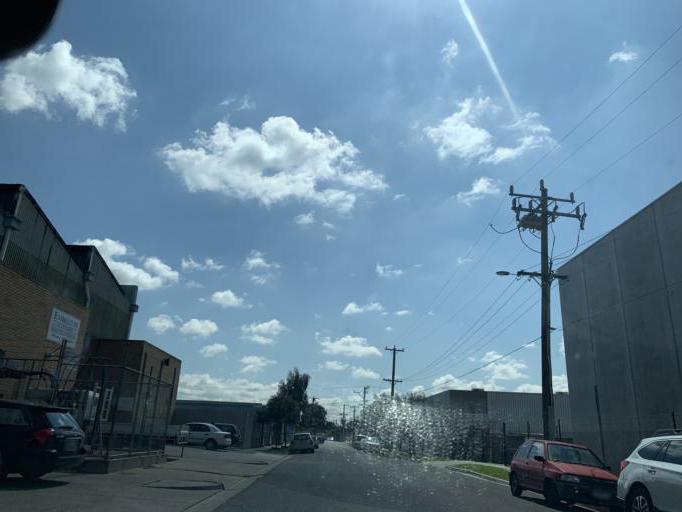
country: AU
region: Victoria
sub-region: Moreland
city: Coburg North
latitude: -37.7270
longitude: 144.9515
